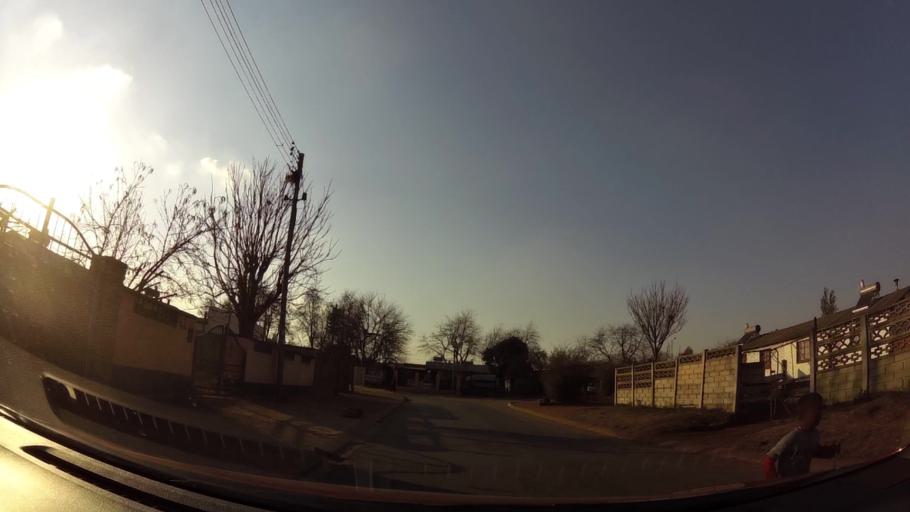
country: ZA
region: Gauteng
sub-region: City of Johannesburg Metropolitan Municipality
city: Soweto
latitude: -26.2935
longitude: 27.8925
